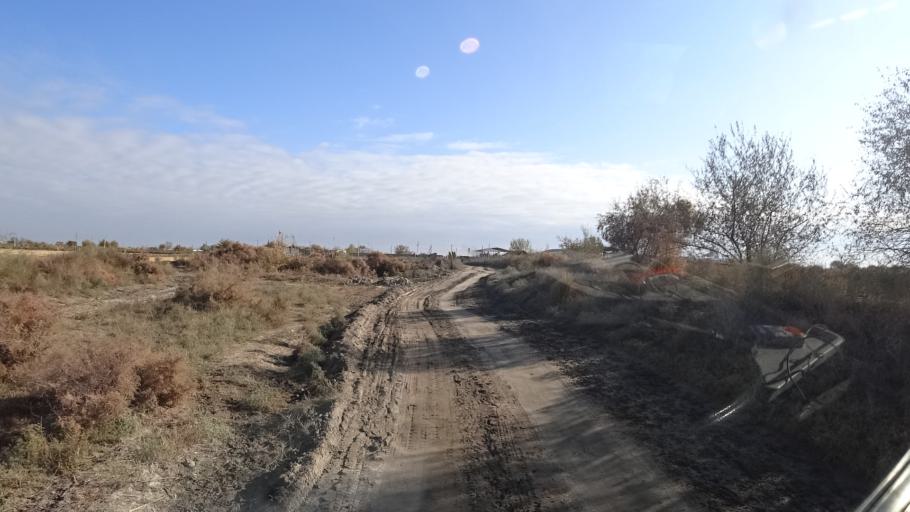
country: UZ
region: Sirdaryo
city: Sirdaryo
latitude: 40.9067
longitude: 68.6783
